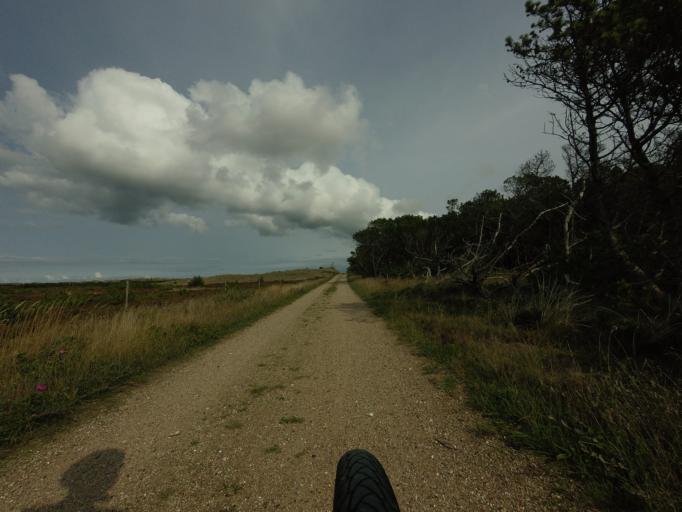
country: DK
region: North Denmark
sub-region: Frederikshavn Kommune
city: Strandby
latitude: 57.6352
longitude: 10.3996
